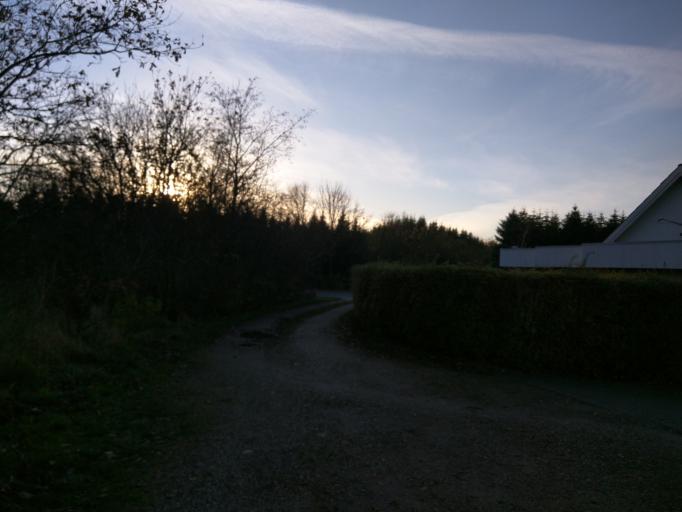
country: DK
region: Central Jutland
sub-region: Viborg Kommune
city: Viborg
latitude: 56.4362
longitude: 9.3707
